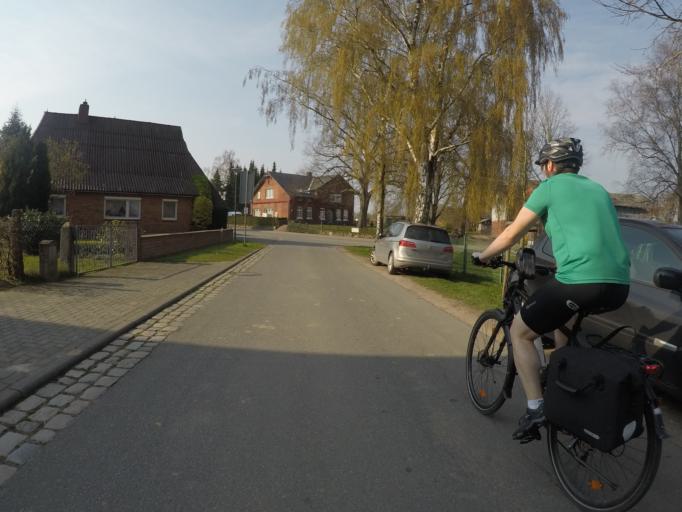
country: DE
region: Schleswig-Holstein
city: Leezen
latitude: 53.8704
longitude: 10.2467
